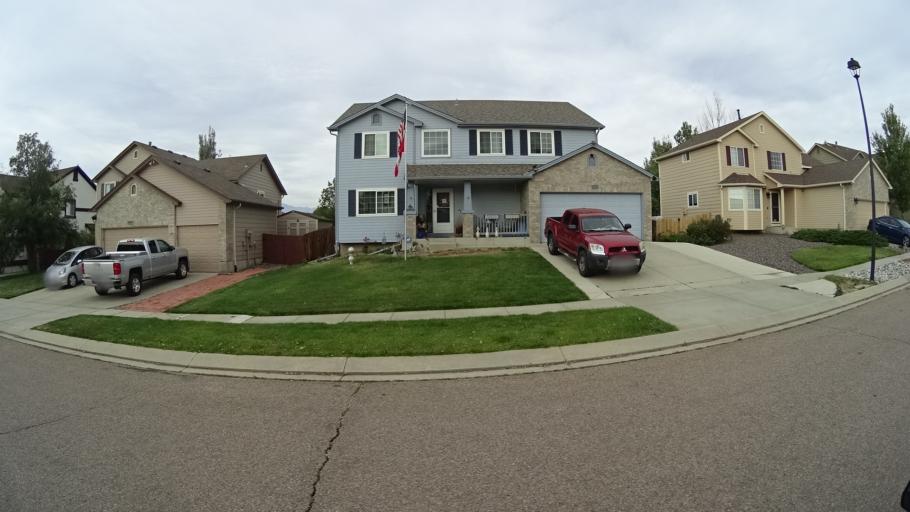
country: US
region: Colorado
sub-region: El Paso County
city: Cimarron Hills
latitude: 38.9158
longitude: -104.7068
